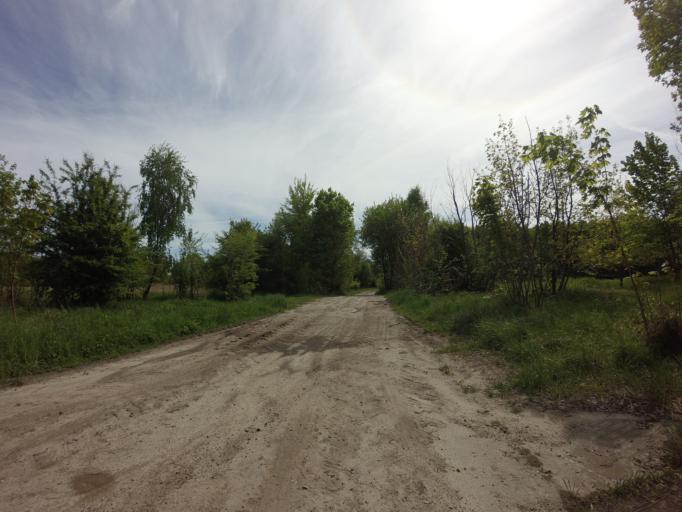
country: PL
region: West Pomeranian Voivodeship
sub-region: Powiat choszczenski
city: Recz
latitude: 53.1684
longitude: 15.5772
